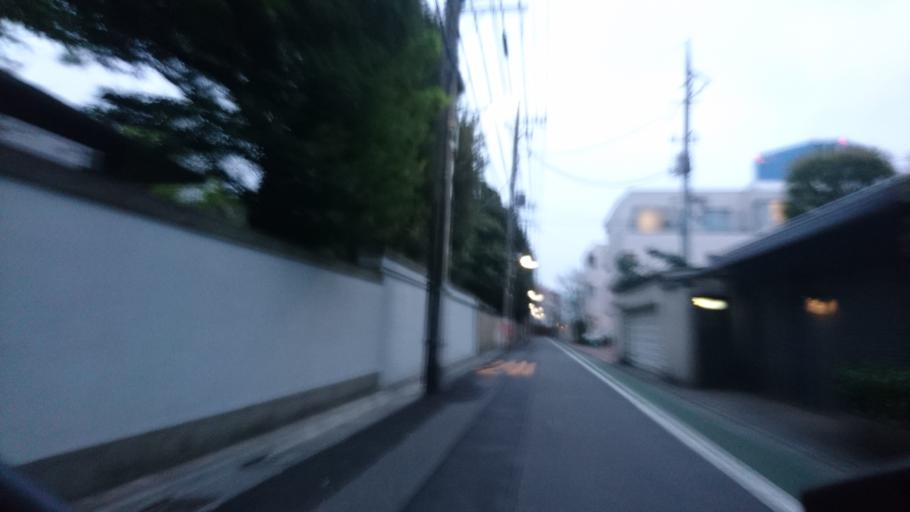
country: JP
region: Tokyo
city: Tokyo
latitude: 35.6216
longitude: 139.7356
